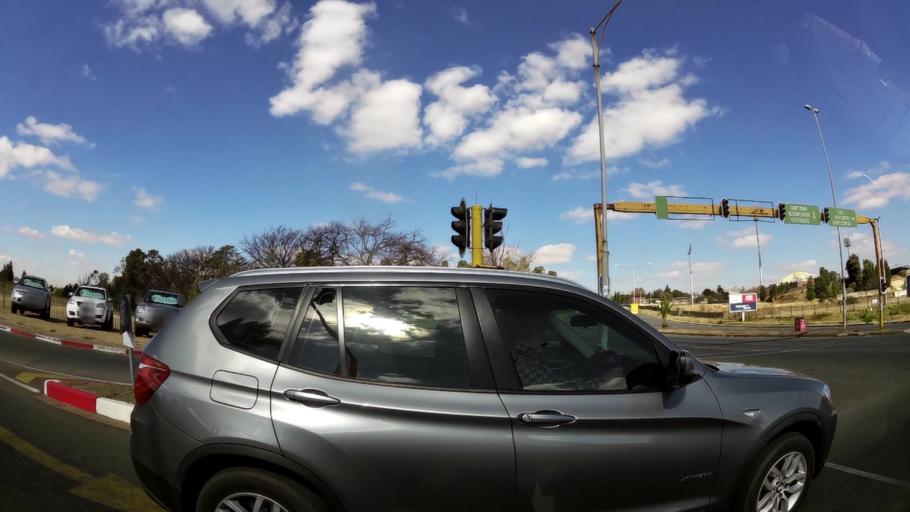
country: ZA
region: Gauteng
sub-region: West Rand District Municipality
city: Krugersdorp
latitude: -26.1001
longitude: 27.7802
